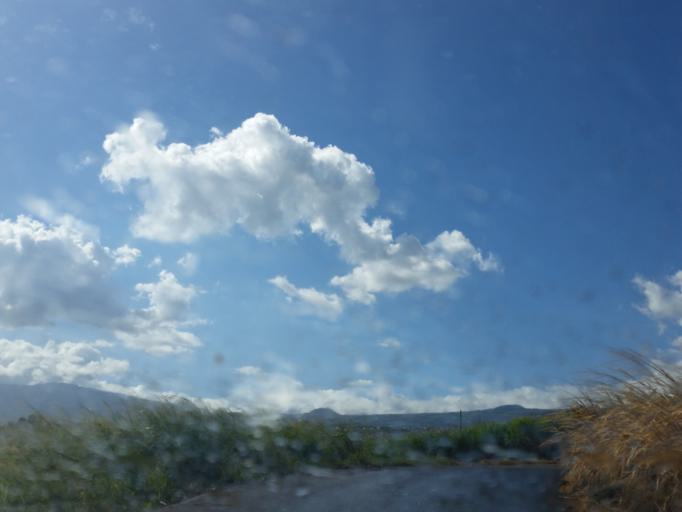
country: RE
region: Reunion
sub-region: Reunion
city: Saint-Pierre
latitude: -21.3177
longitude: 55.5045
